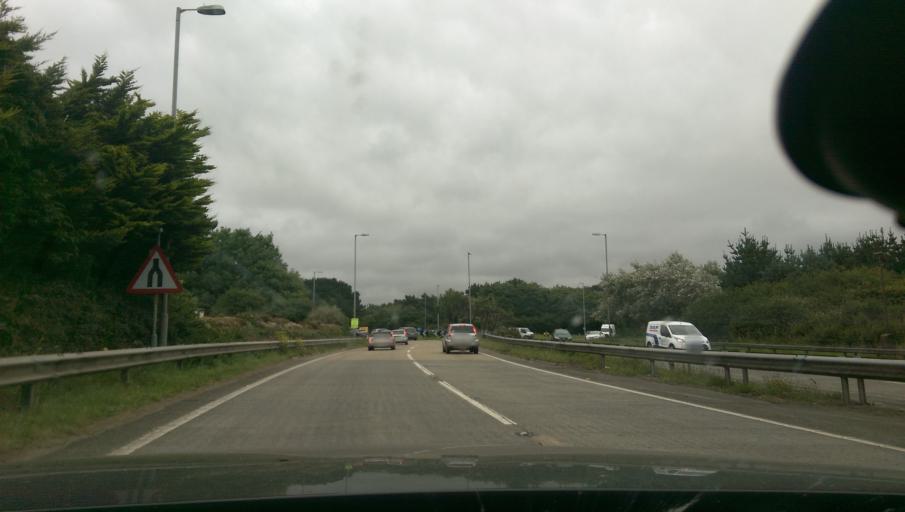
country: GB
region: England
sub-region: Cornwall
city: Marazion
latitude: 50.1345
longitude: -5.4922
